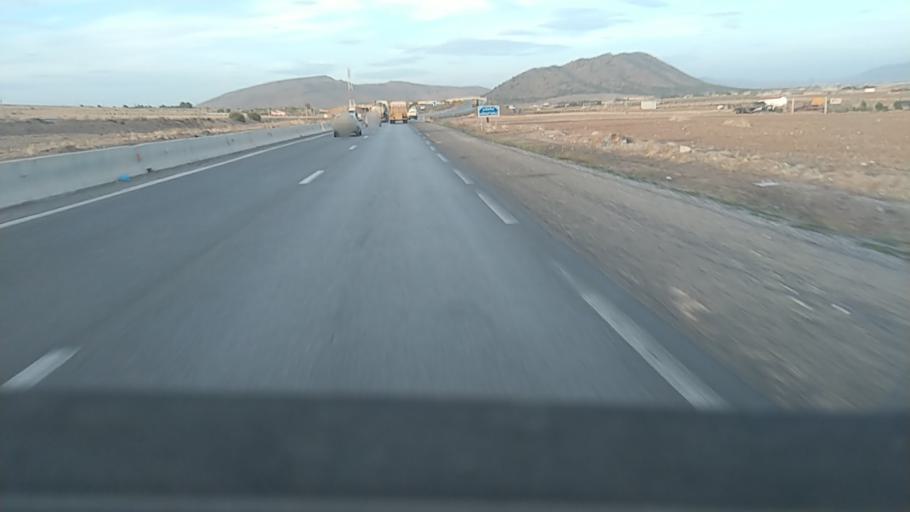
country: DZ
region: Oum el Bouaghi
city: Ain Kercha
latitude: 35.9502
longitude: 6.5245
